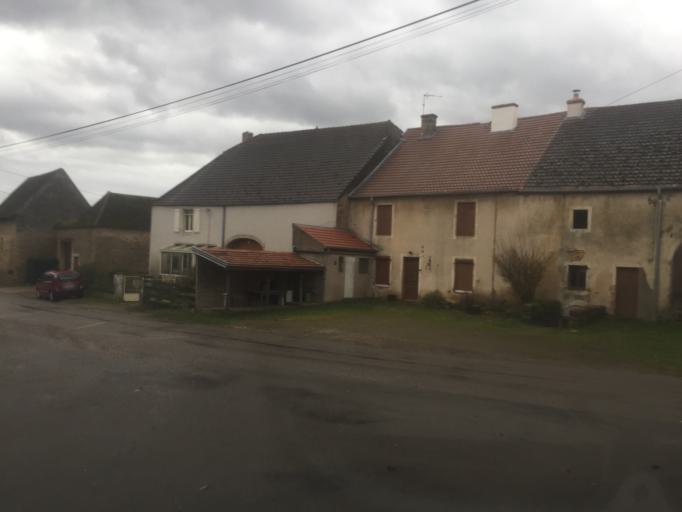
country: FR
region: Franche-Comte
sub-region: Departement de la Haute-Saone
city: Pesmes
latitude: 47.2245
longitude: 5.5007
